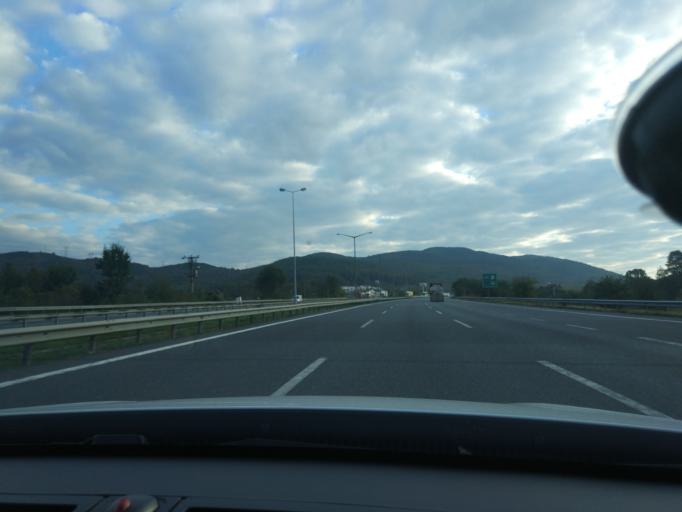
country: TR
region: Sakarya
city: Karadere
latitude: 40.8039
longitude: 30.8526
